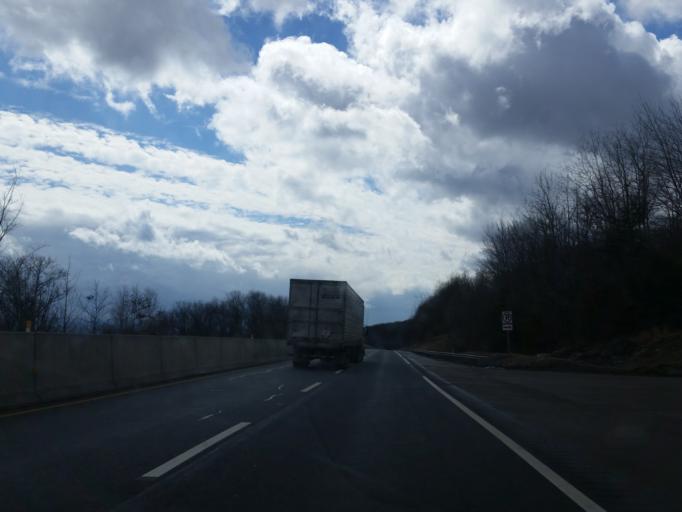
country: US
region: Pennsylvania
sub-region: Lackawanna County
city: Taylor
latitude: 41.4239
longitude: -75.7120
